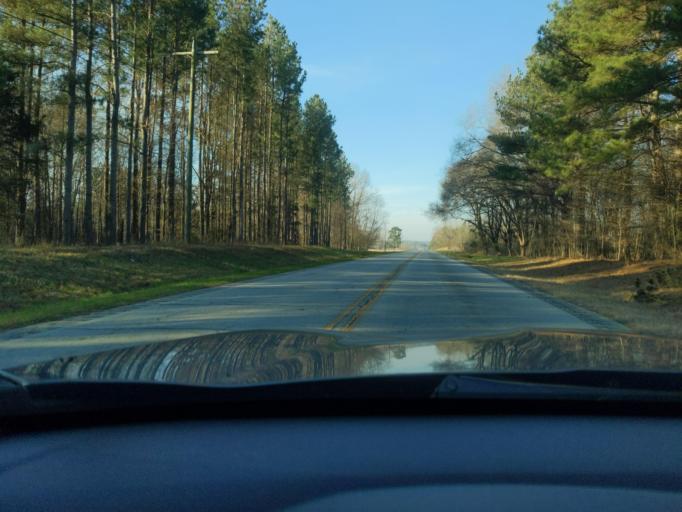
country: US
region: South Carolina
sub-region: Newberry County
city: Newberry
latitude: 34.2165
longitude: -81.7510
